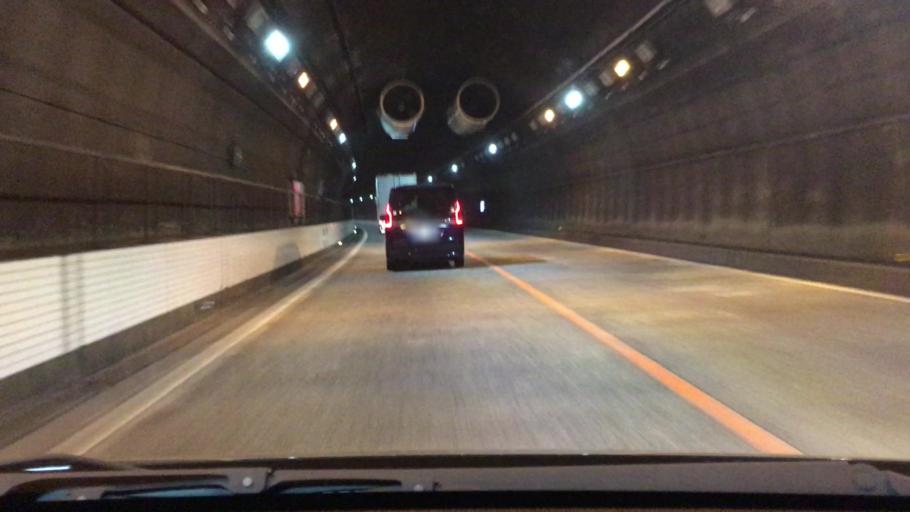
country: JP
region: Yamaguchi
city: Otake
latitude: 34.2116
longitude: 132.1822
